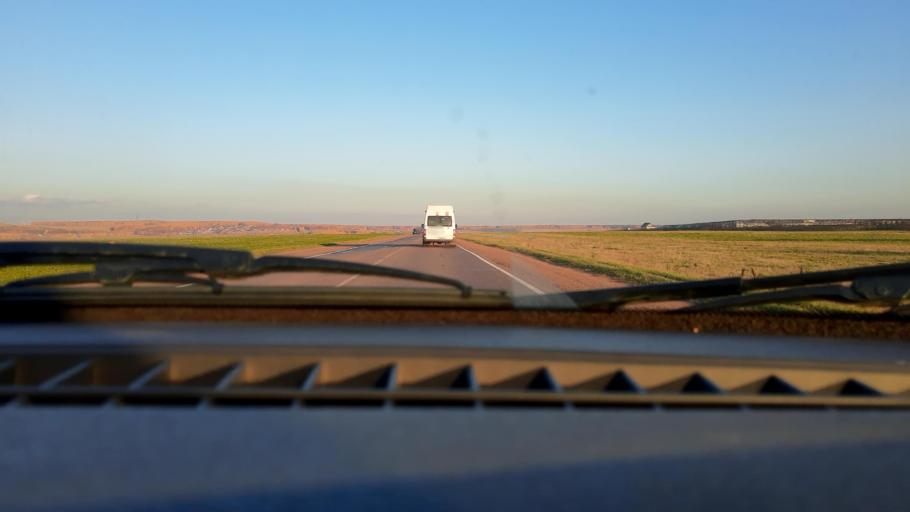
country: RU
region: Bashkortostan
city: Asanovo
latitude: 54.8252
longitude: 55.6466
